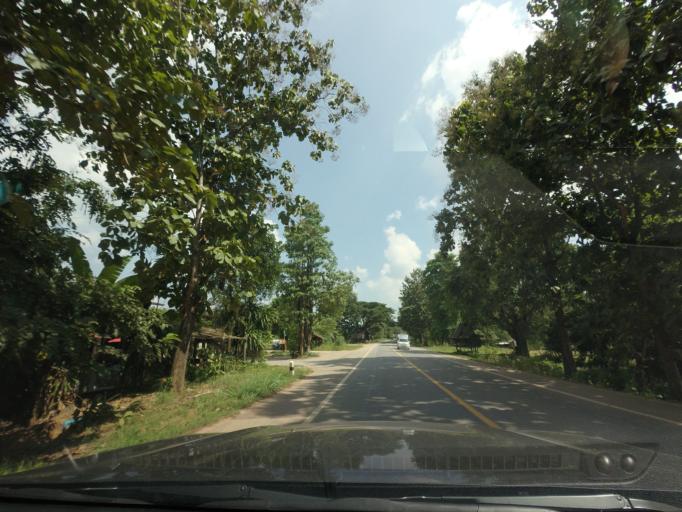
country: TH
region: Phitsanulok
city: Chat Trakan
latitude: 17.2915
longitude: 100.5140
